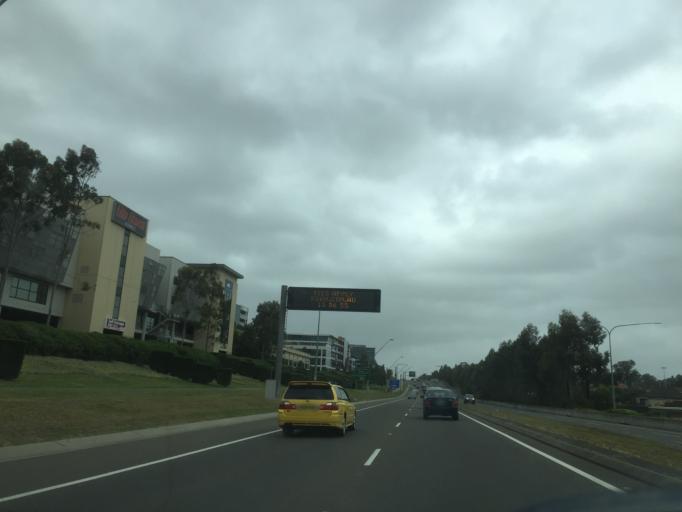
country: AU
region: New South Wales
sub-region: Blacktown
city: Stanhope Gardens
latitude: -33.7338
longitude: 150.9438
